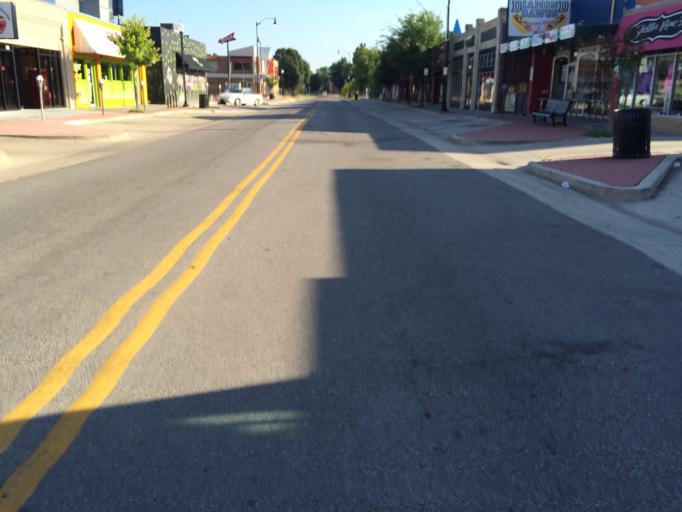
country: US
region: Oklahoma
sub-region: Cleveland County
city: Norman
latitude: 35.2120
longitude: -97.4437
